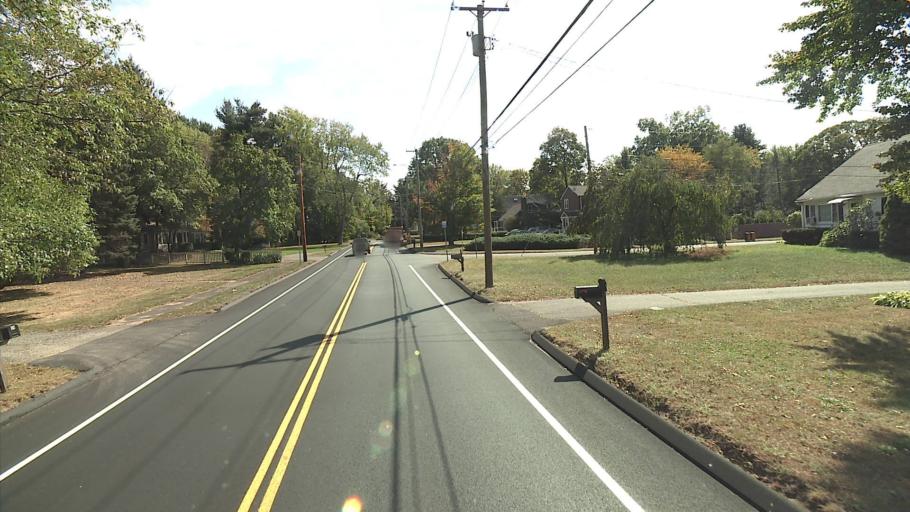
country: US
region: Connecticut
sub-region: New Haven County
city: North Haven
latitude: 41.3840
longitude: -72.8589
